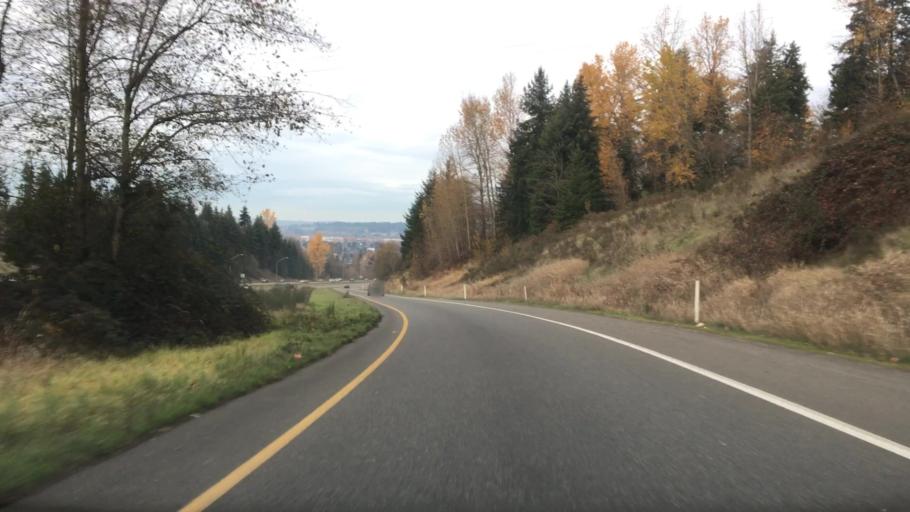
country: US
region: Washington
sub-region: Pierce County
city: Puyallup
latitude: 47.1626
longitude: -122.2956
